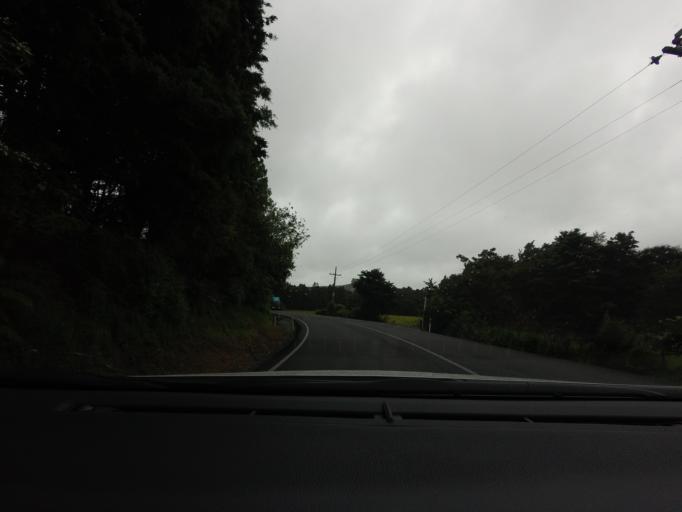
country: NZ
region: Auckland
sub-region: Auckland
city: Wellsford
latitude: -36.2862
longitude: 174.6130
